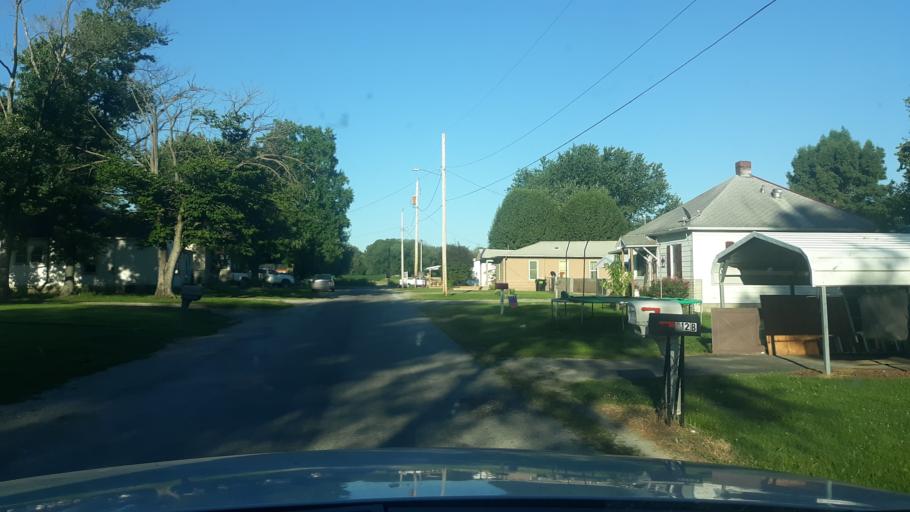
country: US
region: Illinois
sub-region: Saline County
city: Harrisburg
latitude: 37.8432
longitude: -88.6069
